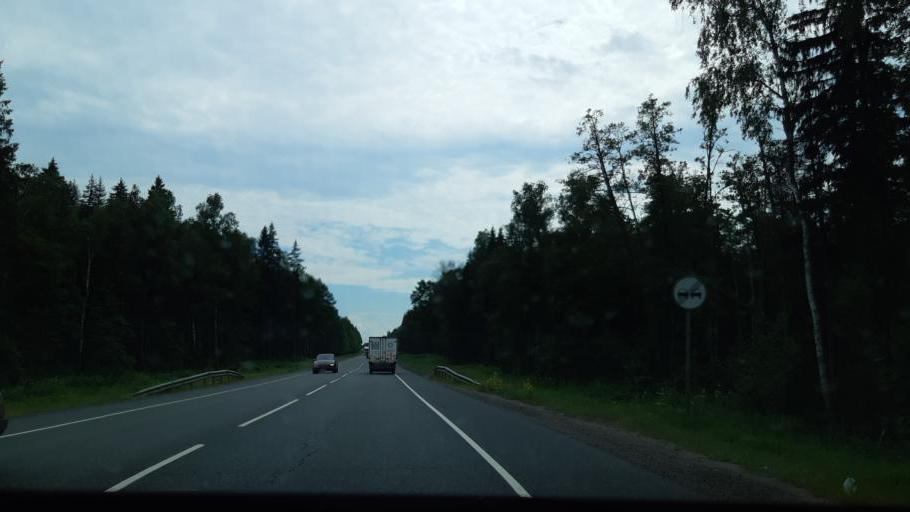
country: RU
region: Moskovskaya
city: Dorokhovo
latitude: 55.4446
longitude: 36.3519
